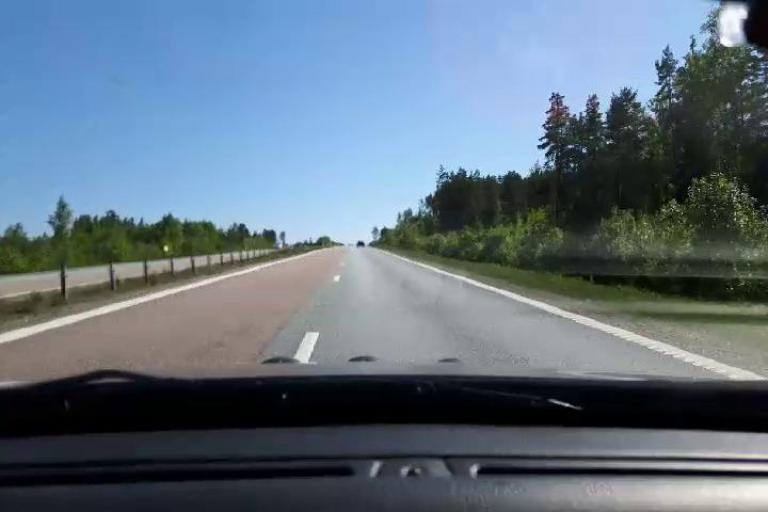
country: SE
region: Gaevleborg
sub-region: Soderhamns Kommun
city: Soderhamn
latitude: 61.3967
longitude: 16.9918
